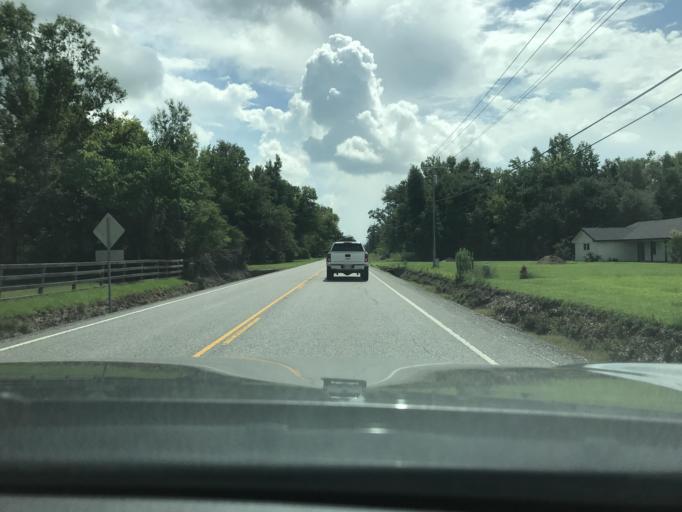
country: US
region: Louisiana
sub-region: Calcasieu Parish
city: Moss Bluff
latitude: 30.3447
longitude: -93.2137
